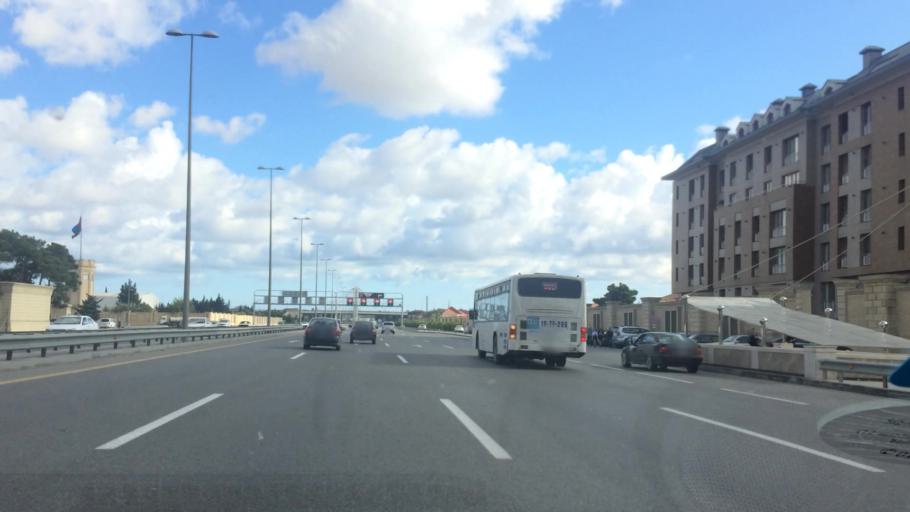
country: AZ
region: Baki
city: Biny Selo
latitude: 40.4555
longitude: 50.0686
